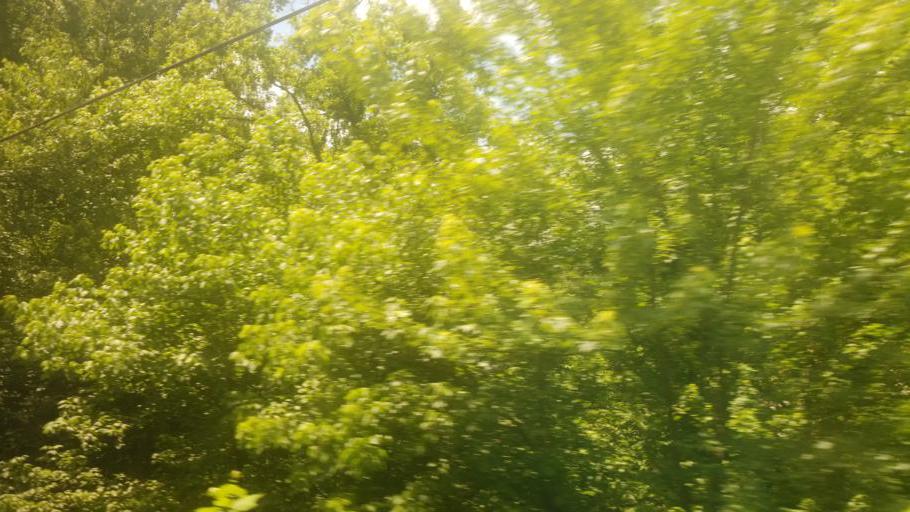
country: US
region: Maryland
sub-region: Frederick County
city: Point of Rocks
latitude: 39.2966
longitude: -77.5573
